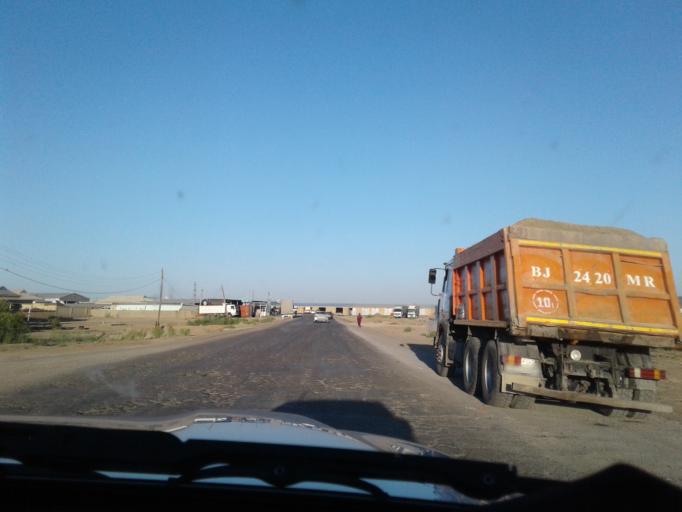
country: TM
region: Mary
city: Mary
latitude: 37.5644
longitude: 61.8204
